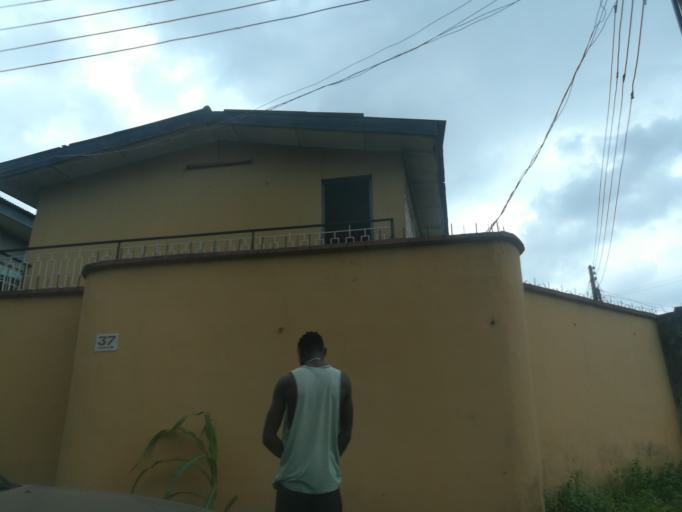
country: NG
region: Lagos
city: Ikeja
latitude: 6.6021
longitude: 3.3480
